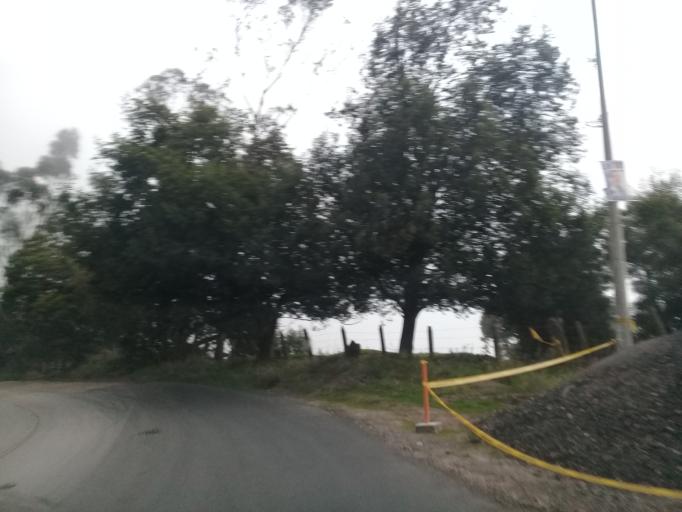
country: CO
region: Cundinamarca
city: Zipaquira
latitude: 5.0886
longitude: -74.0680
